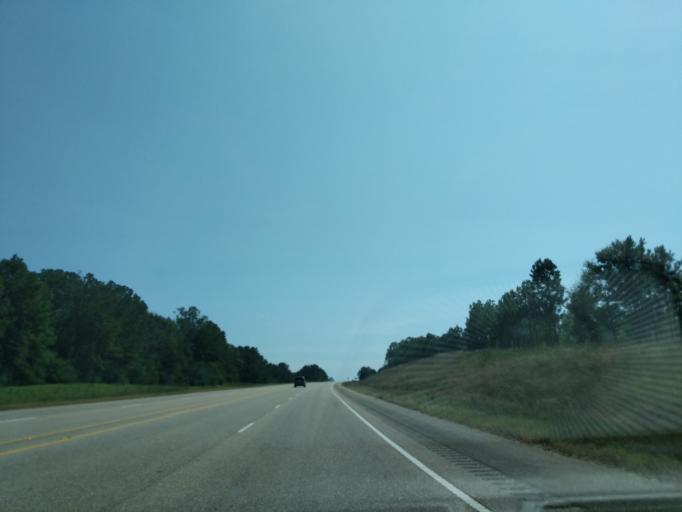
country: US
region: Alabama
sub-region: Butler County
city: Georgiana
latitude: 31.5459
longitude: -86.7327
